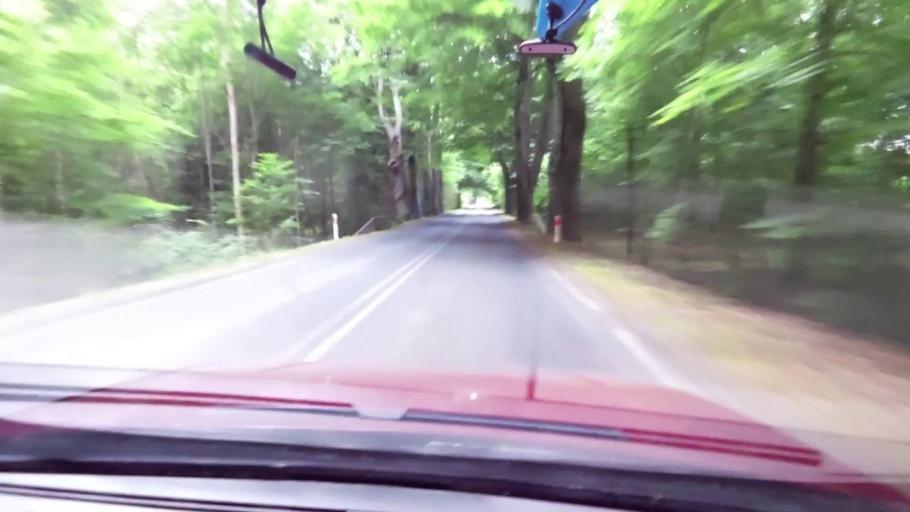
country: PL
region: West Pomeranian Voivodeship
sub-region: Powiat koszalinski
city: Polanow
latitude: 54.1376
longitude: 16.5192
